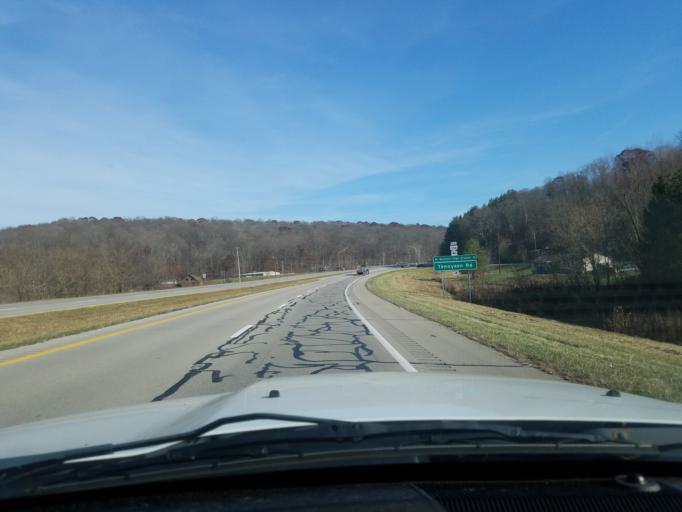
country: US
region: Ohio
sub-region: Pike County
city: Piketon
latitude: 39.0602
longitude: -83.1172
